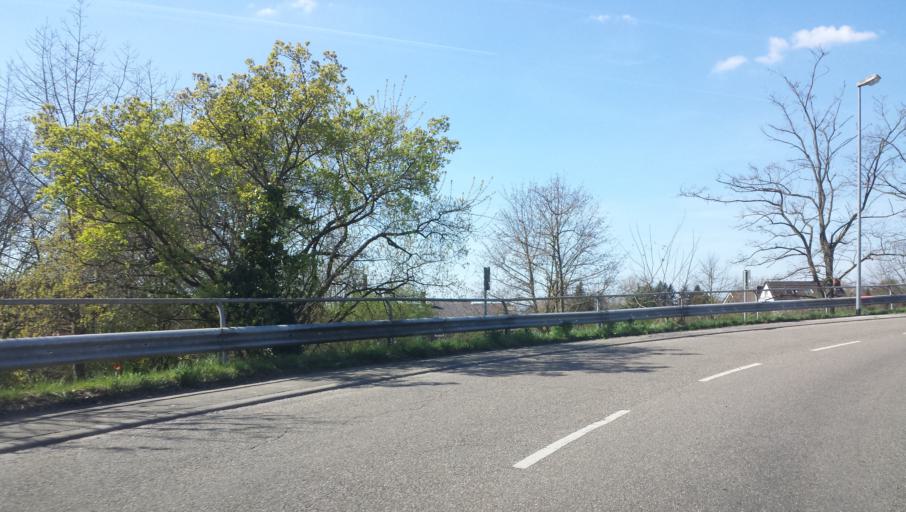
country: DE
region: Rheinland-Pfalz
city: Schifferstadt
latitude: 49.3712
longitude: 8.3817
